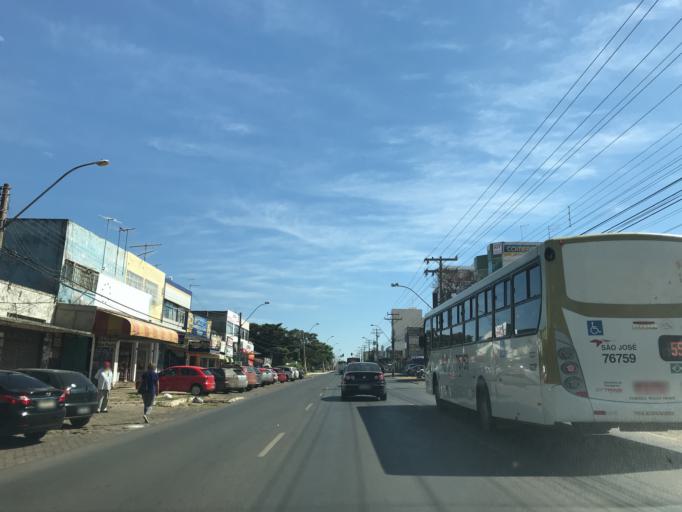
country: BR
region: Federal District
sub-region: Brasilia
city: Brasilia
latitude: -15.8145
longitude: -48.0672
